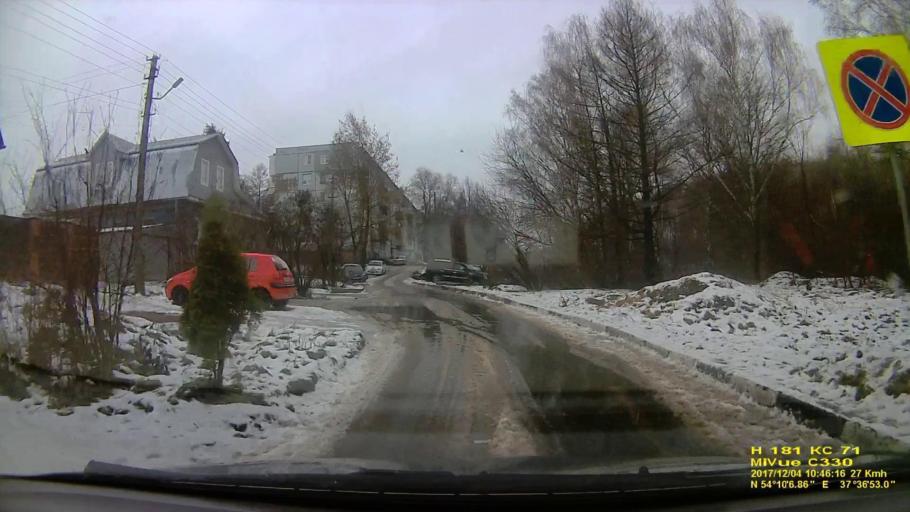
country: RU
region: Tula
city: Tula
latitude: 54.1687
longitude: 37.6146
